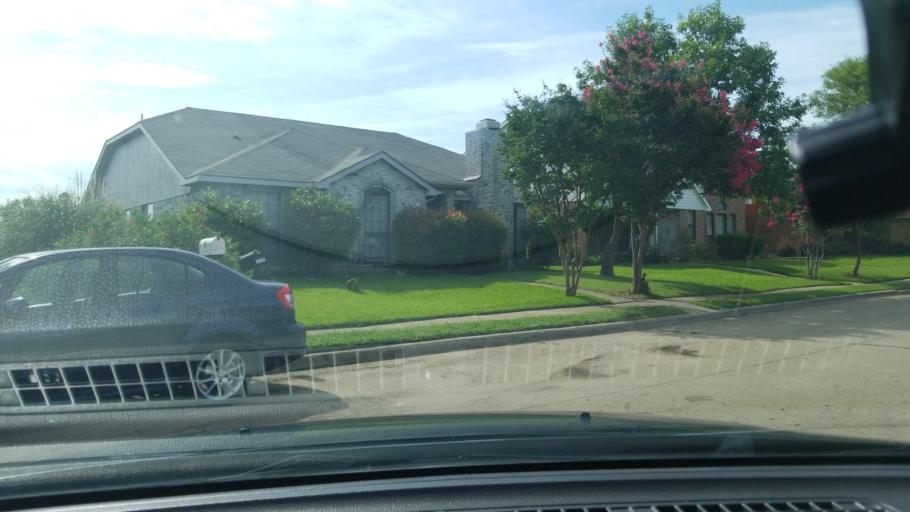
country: US
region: Texas
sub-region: Dallas County
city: Balch Springs
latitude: 32.7760
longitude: -96.6605
